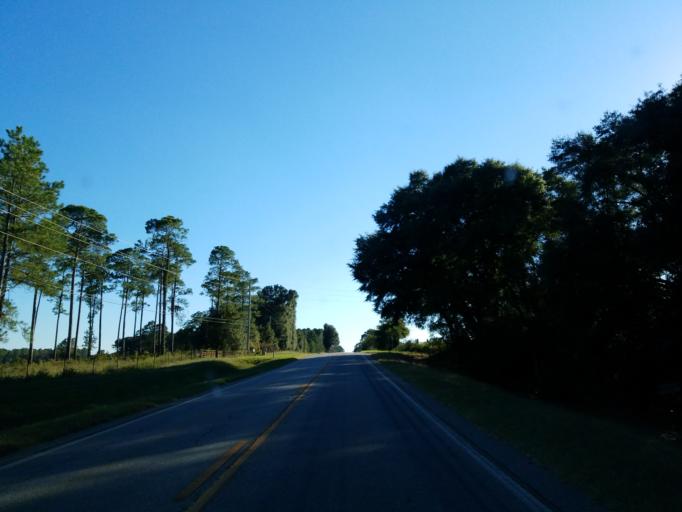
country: US
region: Georgia
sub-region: Lee County
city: Leesburg
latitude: 31.7728
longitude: -84.1416
